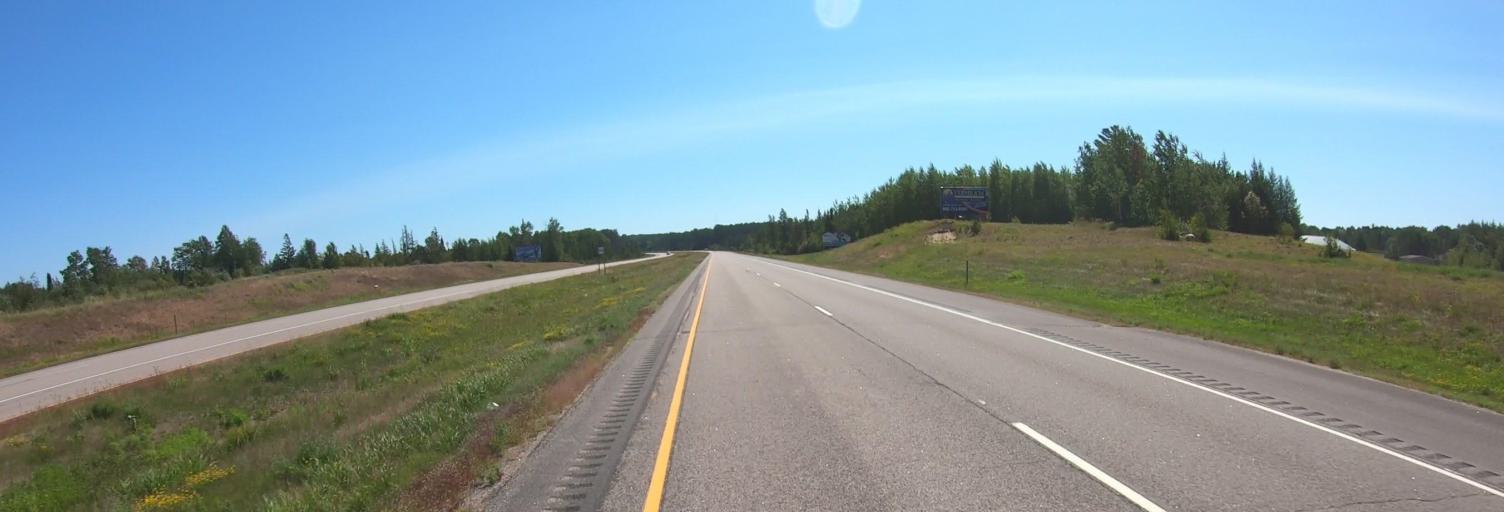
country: US
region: Minnesota
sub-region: Saint Louis County
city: Mountain Iron
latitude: 47.6629
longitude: -92.6296
